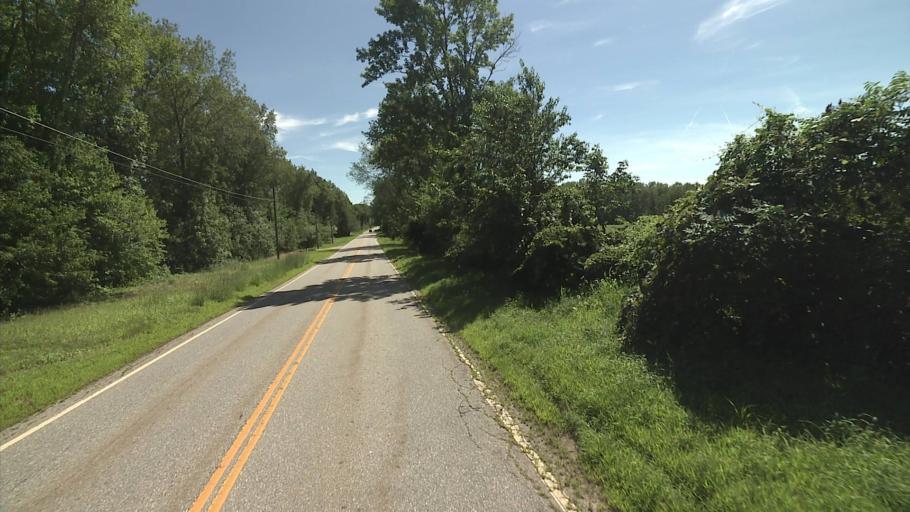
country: US
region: Connecticut
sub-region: Windham County
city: Windham
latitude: 41.7131
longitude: -72.0680
